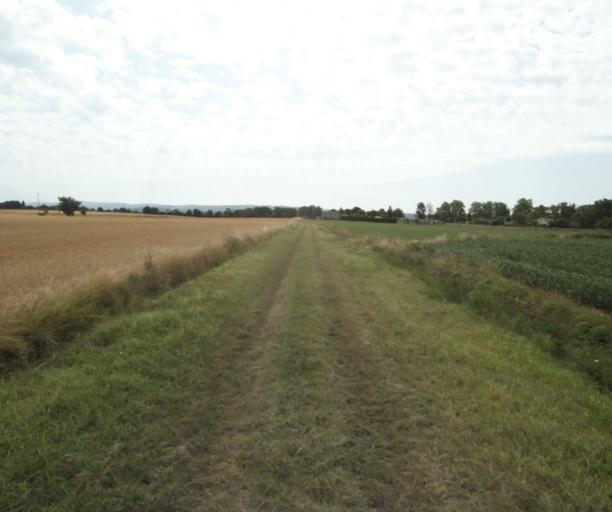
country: FR
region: Midi-Pyrenees
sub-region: Departement de la Haute-Garonne
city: Saint-Felix-Lauragais
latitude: 43.4496
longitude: 1.9274
